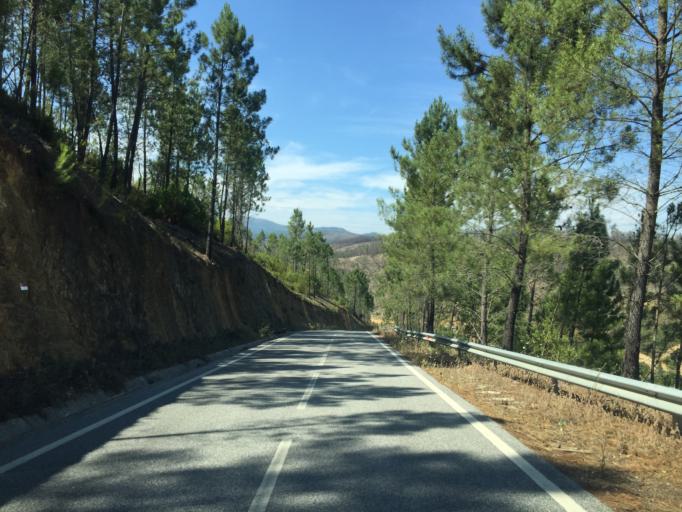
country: PT
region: Castelo Branco
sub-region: Oleiros
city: Oleiros
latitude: 40.0056
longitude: -7.8403
